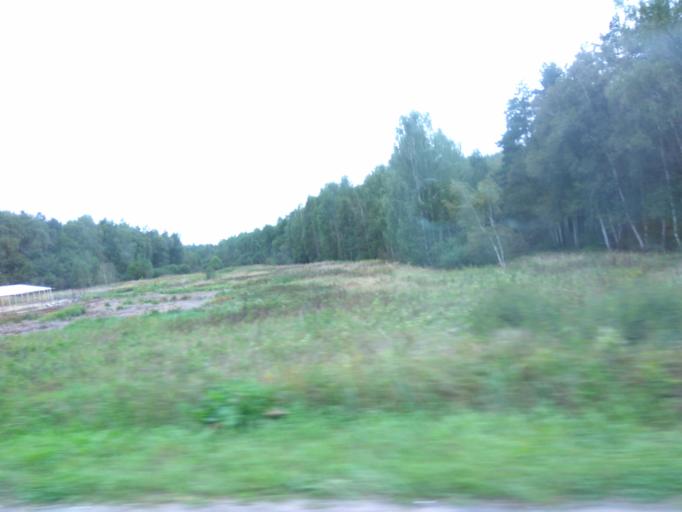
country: RU
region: Moskovskaya
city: Malyshevo
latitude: 55.5196
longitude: 38.3430
